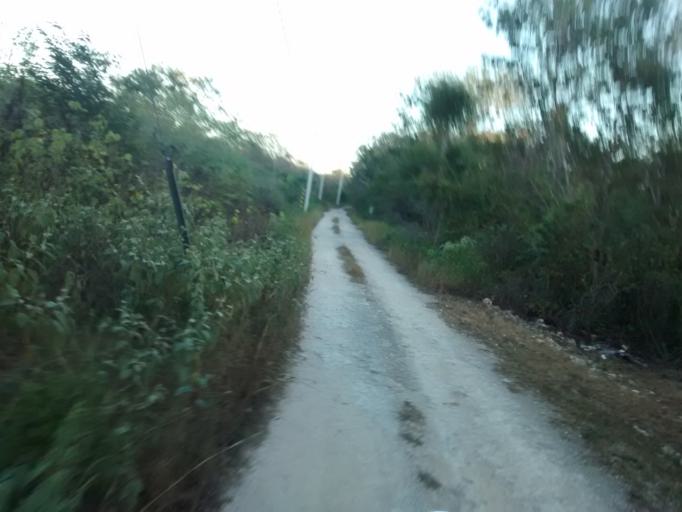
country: MX
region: Yucatan
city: Chichimila
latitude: 20.4469
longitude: -88.1970
